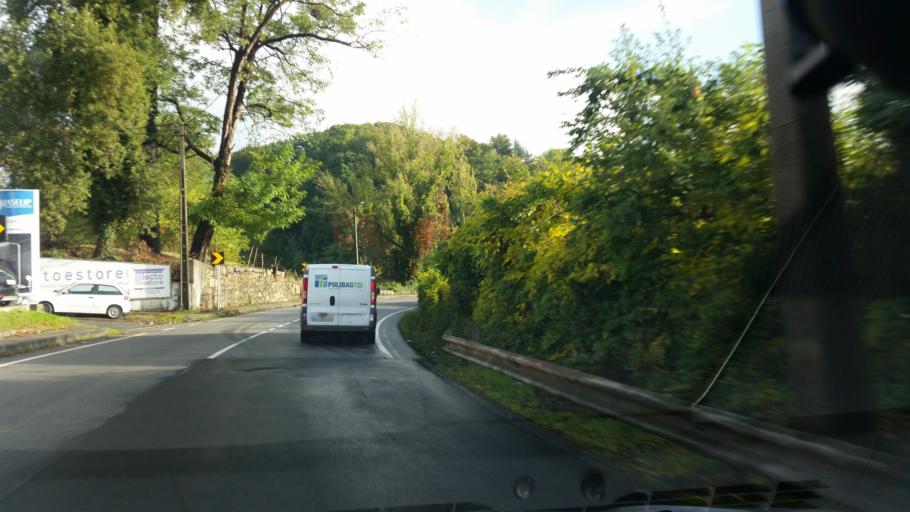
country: PT
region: Braga
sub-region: Guimaraes
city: Lordelo
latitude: 41.3699
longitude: -8.3811
